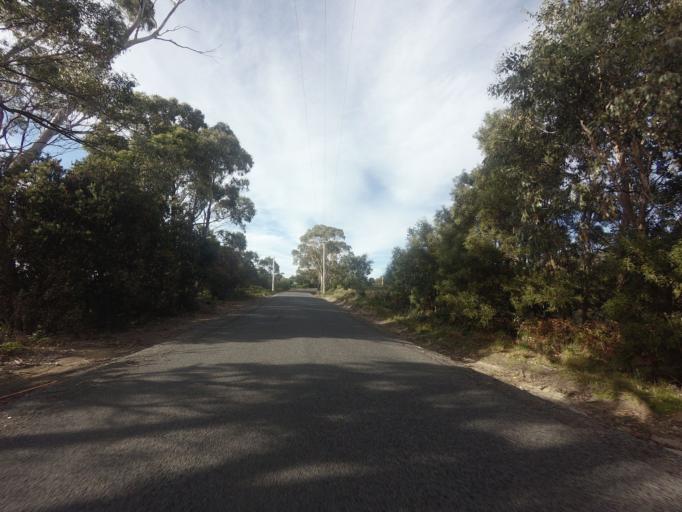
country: AU
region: Tasmania
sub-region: Sorell
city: Sorell
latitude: -42.9646
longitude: 147.8321
